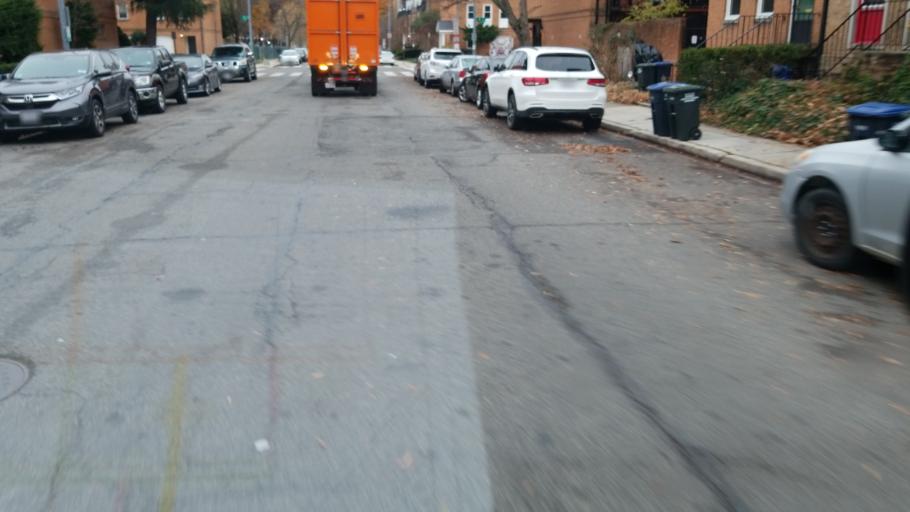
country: US
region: Washington, D.C.
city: Washington, D.C.
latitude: 38.8809
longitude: -77.0199
